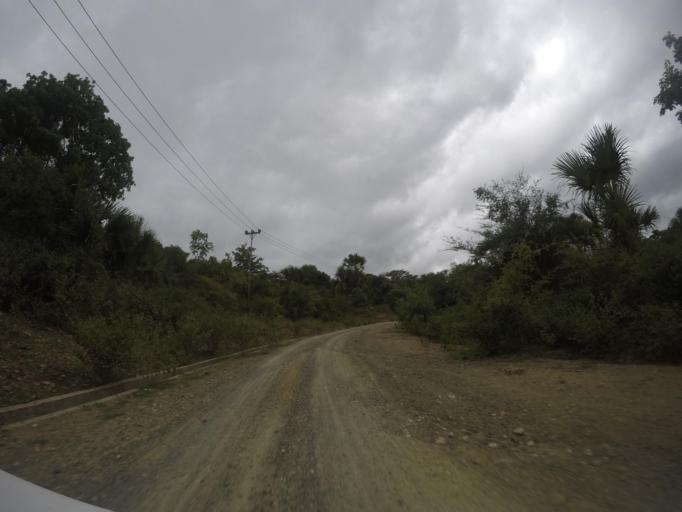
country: TL
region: Bobonaro
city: Maliana
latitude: -8.8500
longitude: 125.0707
